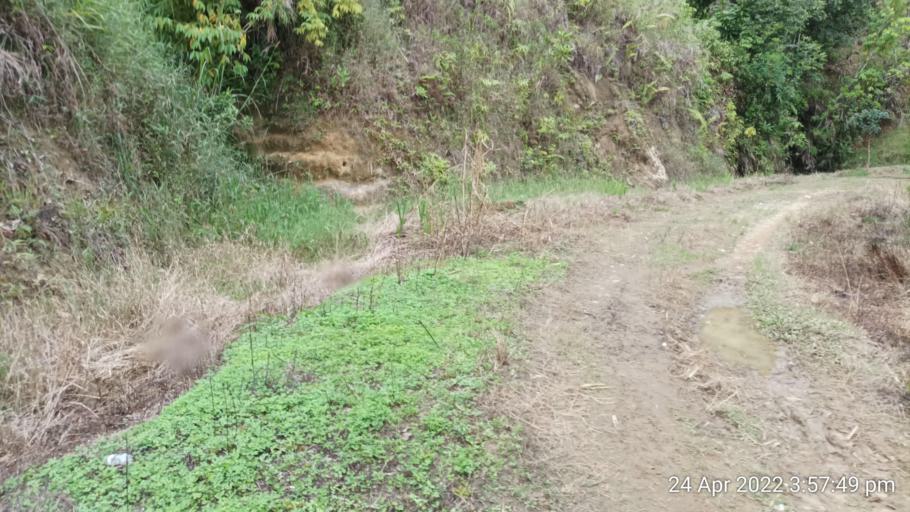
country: PG
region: Jiwaka
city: Minj
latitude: -5.8996
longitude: 144.8236
